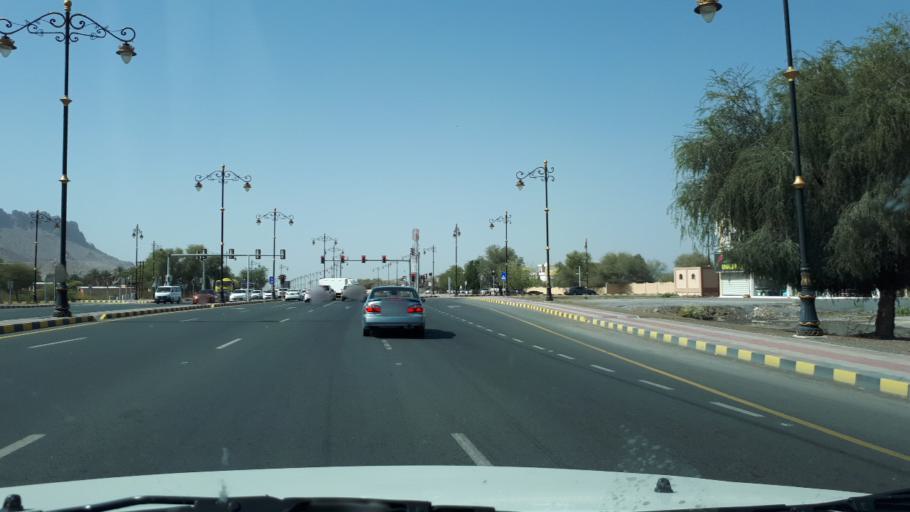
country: OM
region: Muhafazat ad Dakhiliyah
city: Nizwa
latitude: 22.9223
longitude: 57.5370
